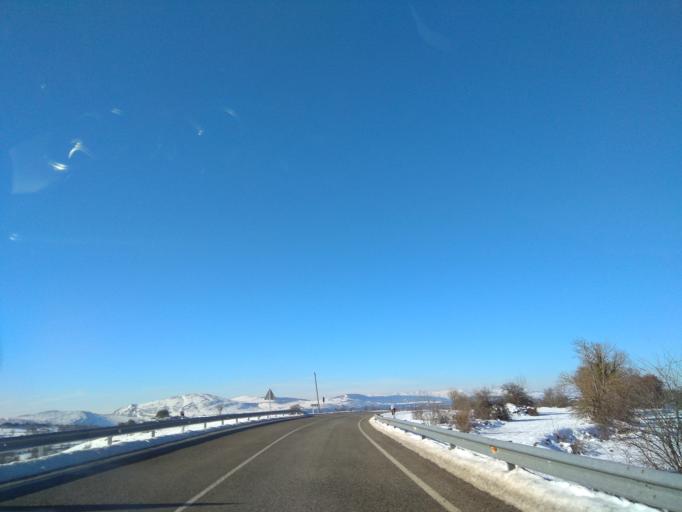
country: ES
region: Cantabria
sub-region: Provincia de Cantabria
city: San Martin de Elines
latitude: 42.9358
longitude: -3.7212
